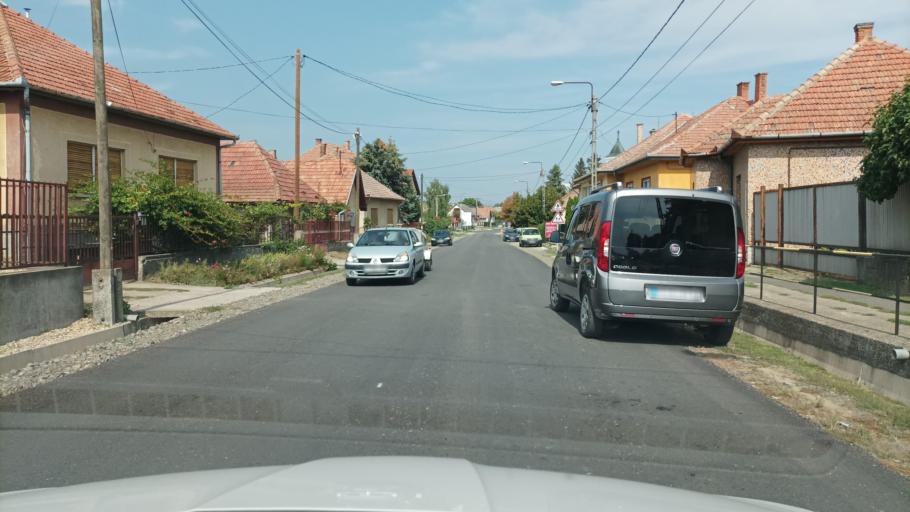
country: HU
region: Pest
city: Tura
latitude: 47.6105
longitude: 19.5967
